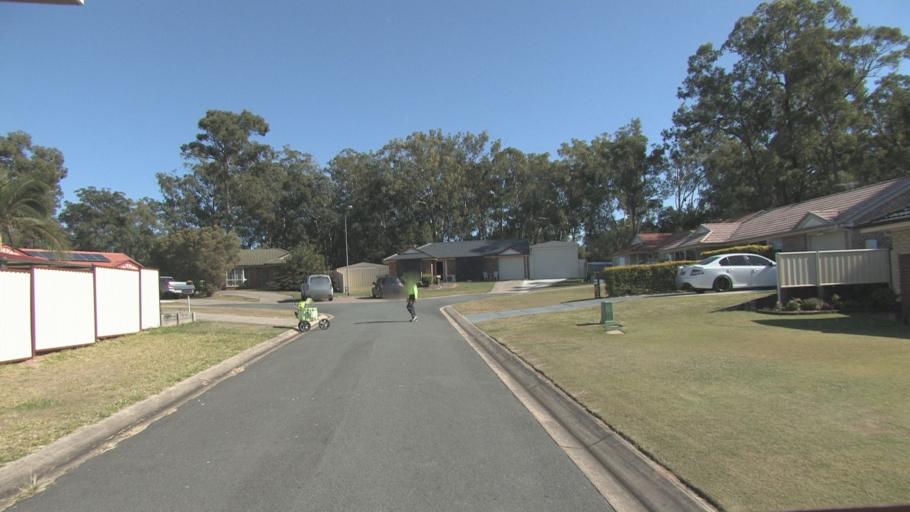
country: AU
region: Queensland
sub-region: Logan
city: Park Ridge South
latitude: -27.6735
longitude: 153.0201
